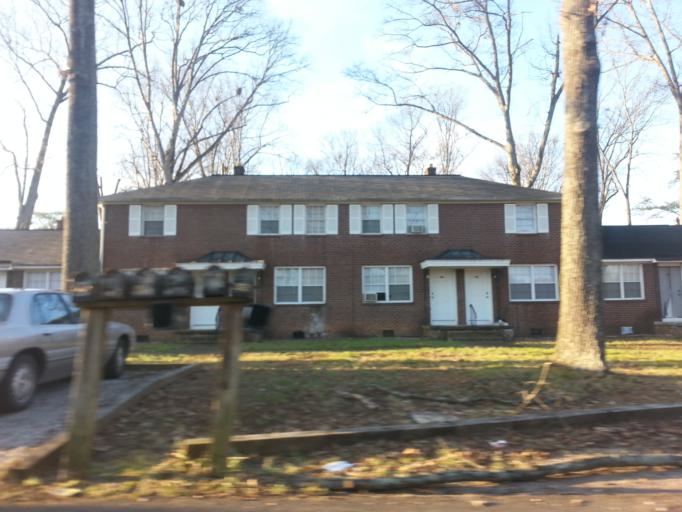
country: US
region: Tennessee
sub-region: Knox County
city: Knoxville
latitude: 36.0155
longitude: -83.9024
